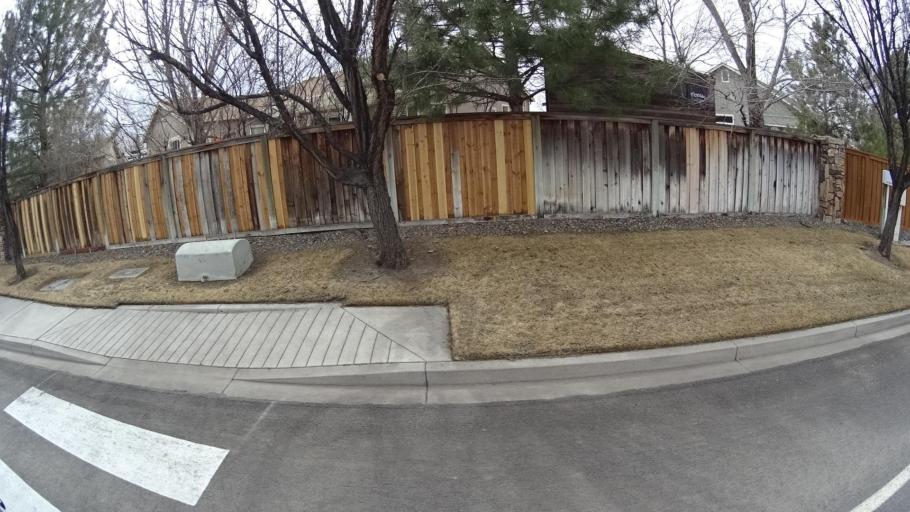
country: US
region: Nevada
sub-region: Washoe County
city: Spanish Springs
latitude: 39.6306
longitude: -119.6921
